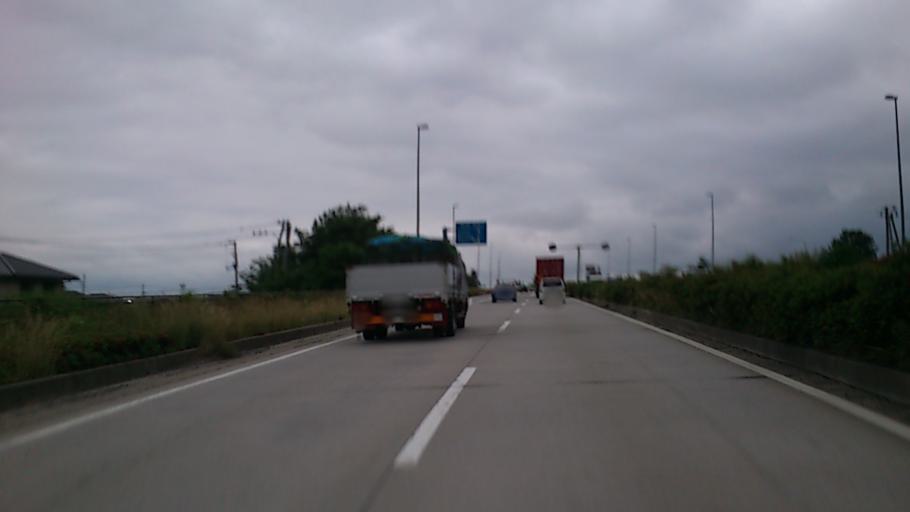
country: JP
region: Fukushima
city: Koriyama
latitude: 37.4292
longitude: 140.3636
